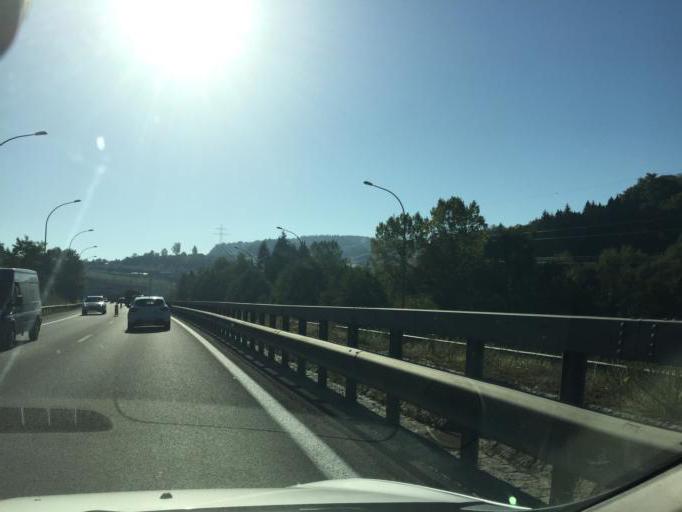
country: LU
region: Luxembourg
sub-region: Canton de Mersch
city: Mersch
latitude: 49.7342
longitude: 6.1004
